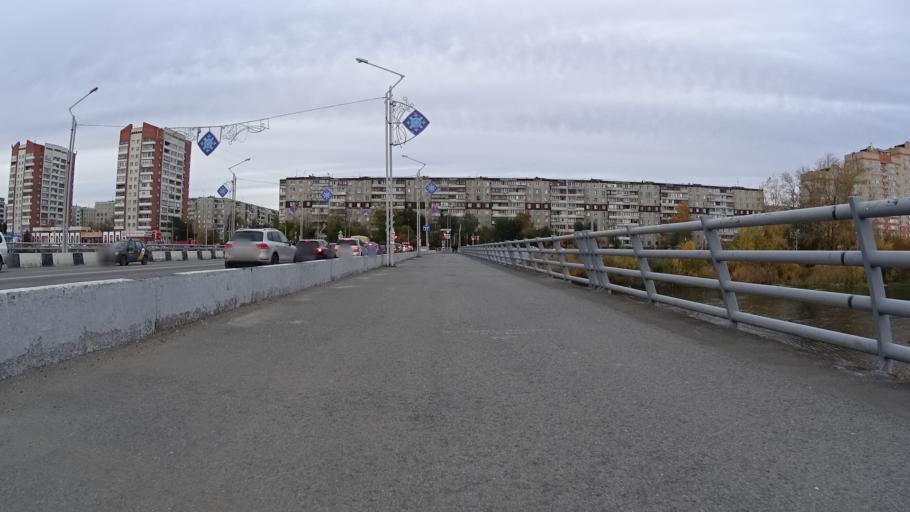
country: RU
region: Chelyabinsk
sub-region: Gorod Chelyabinsk
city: Chelyabinsk
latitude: 55.1733
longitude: 61.3490
